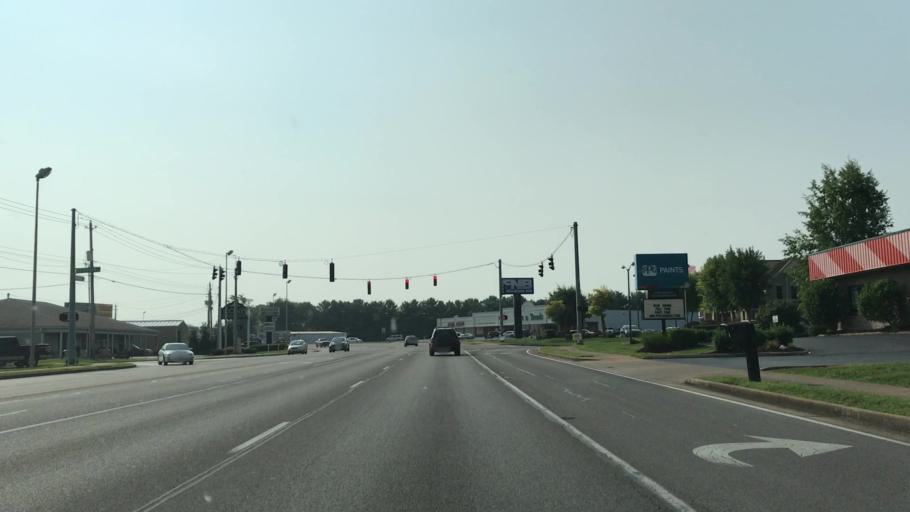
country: US
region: Kentucky
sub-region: Warren County
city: Bowling Green
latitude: 36.9521
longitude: -86.4421
